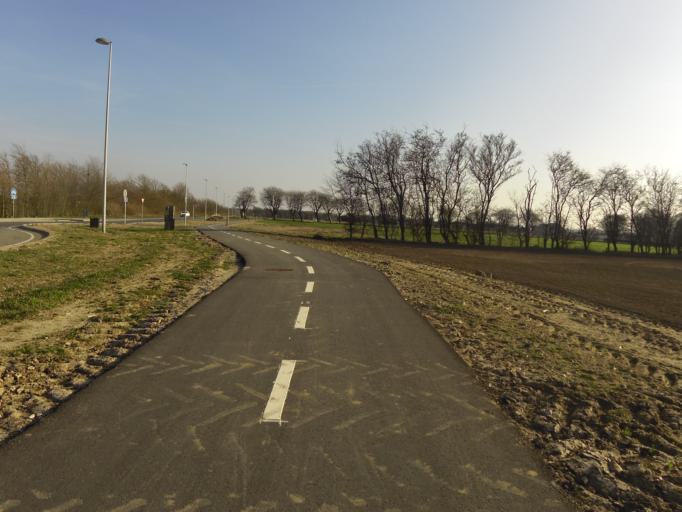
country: DK
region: South Denmark
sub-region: Vejen Kommune
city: Vejen
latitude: 55.4607
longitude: 9.1066
